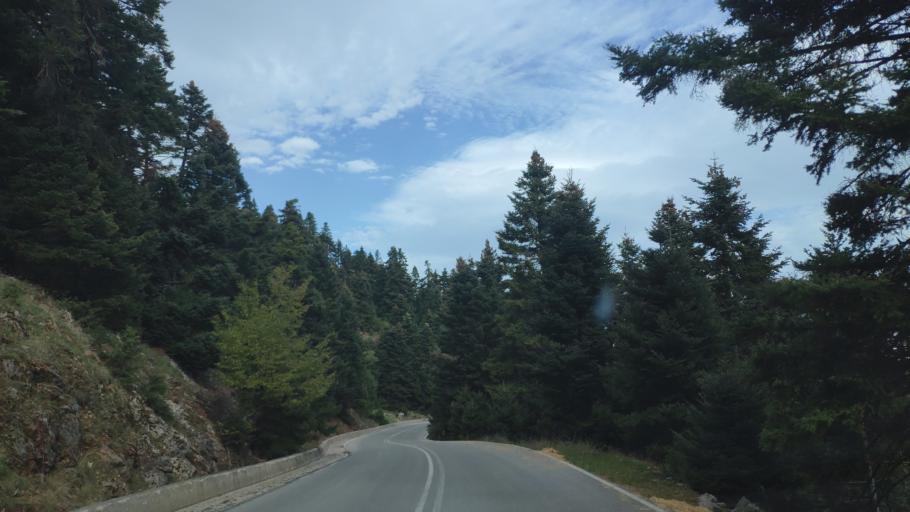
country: GR
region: Central Greece
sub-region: Nomos Fokidos
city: Amfissa
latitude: 38.6597
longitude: 22.3811
